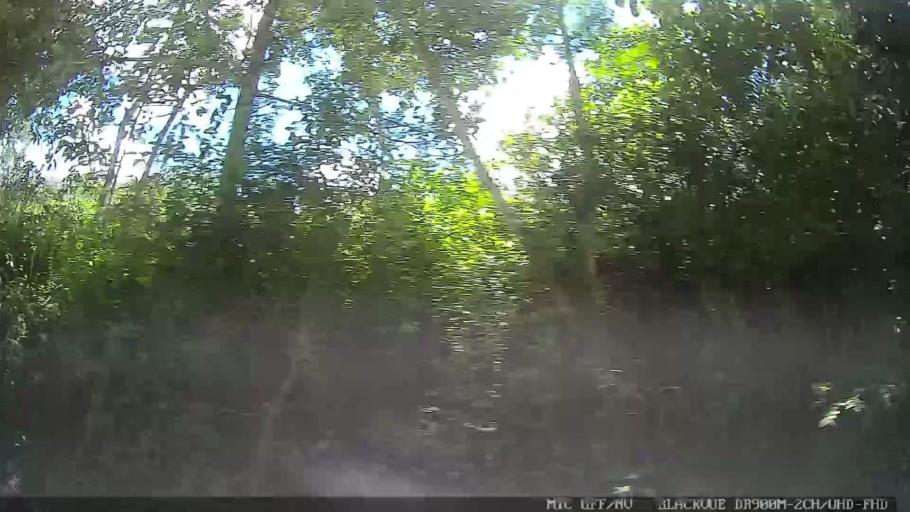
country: BR
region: Sao Paulo
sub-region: Santa Branca
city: Santa Branca
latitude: -23.5295
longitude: -45.7147
